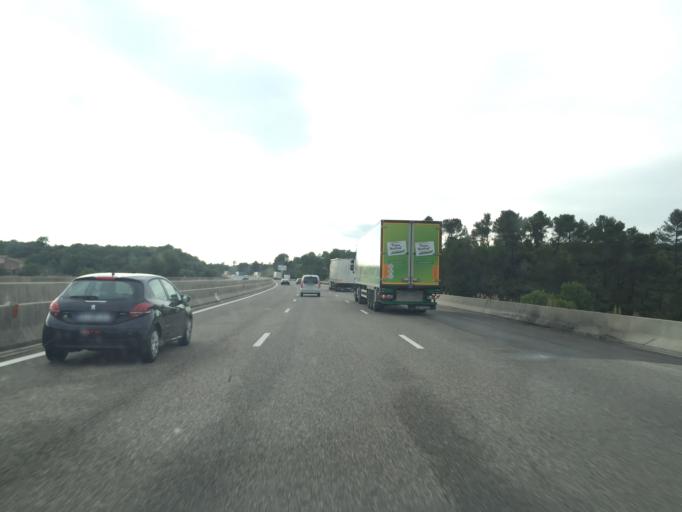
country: FR
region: Provence-Alpes-Cote d'Azur
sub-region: Departement du Var
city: Saint-Maximin-la-Sainte-Baume
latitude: 43.4430
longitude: 5.9025
